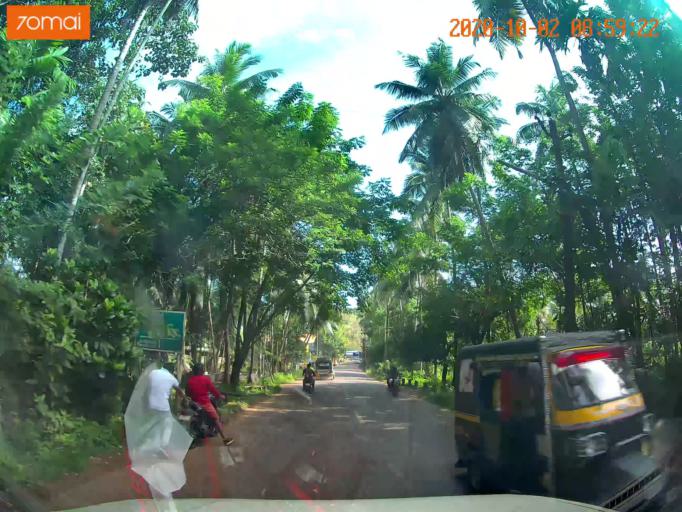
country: IN
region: Kerala
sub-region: Kozhikode
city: Naduvannur
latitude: 11.4478
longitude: 75.7732
